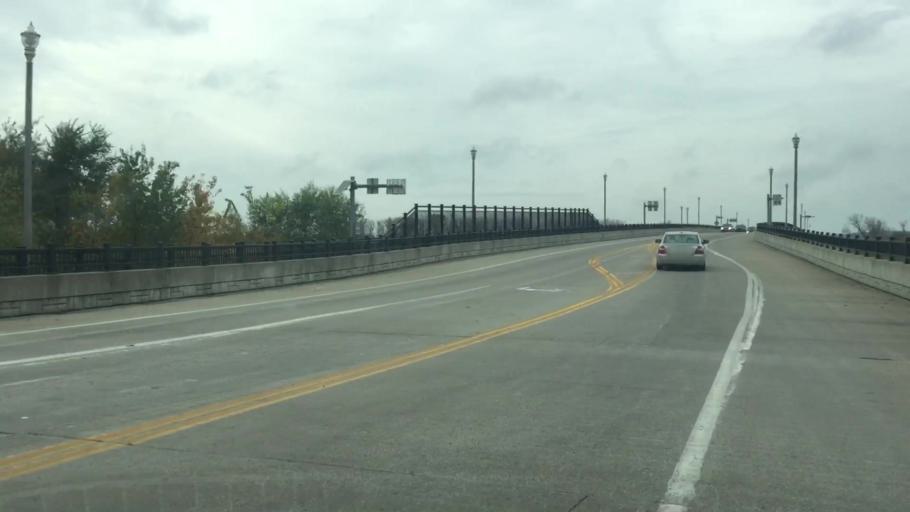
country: US
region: Missouri
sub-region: Gasconade County
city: Hermann
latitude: 38.7071
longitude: -91.4377
